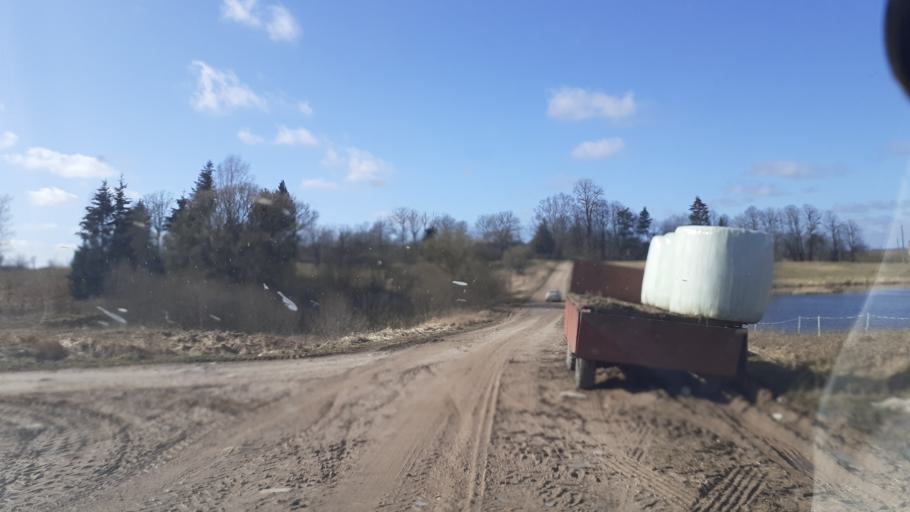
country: LV
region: Kuldigas Rajons
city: Kuldiga
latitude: 56.9336
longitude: 22.1609
